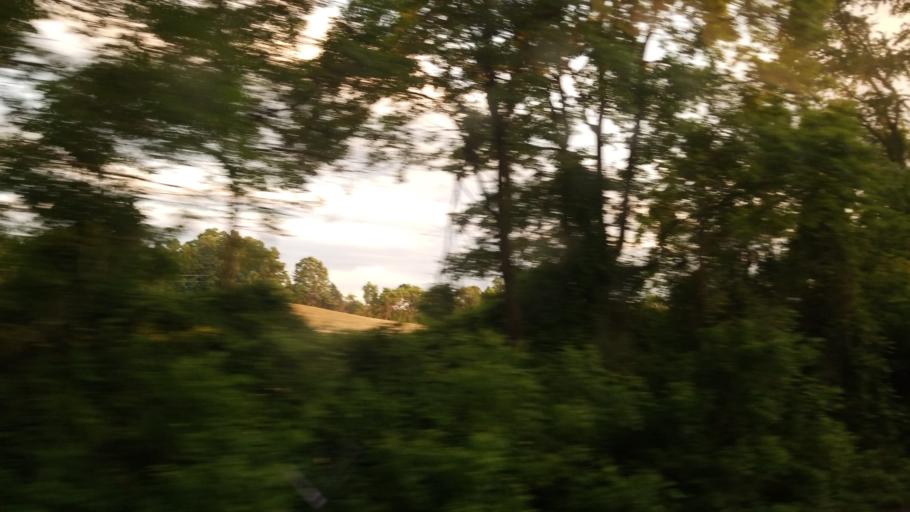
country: US
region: Virginia
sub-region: Culpeper County
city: Culpeper
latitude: 38.4816
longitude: -77.9628
